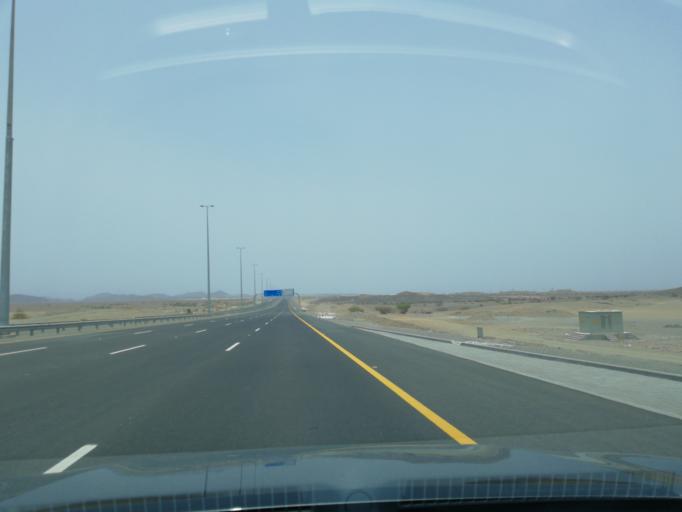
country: OM
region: Al Batinah
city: Al Liwa'
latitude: 24.4321
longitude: 56.5262
